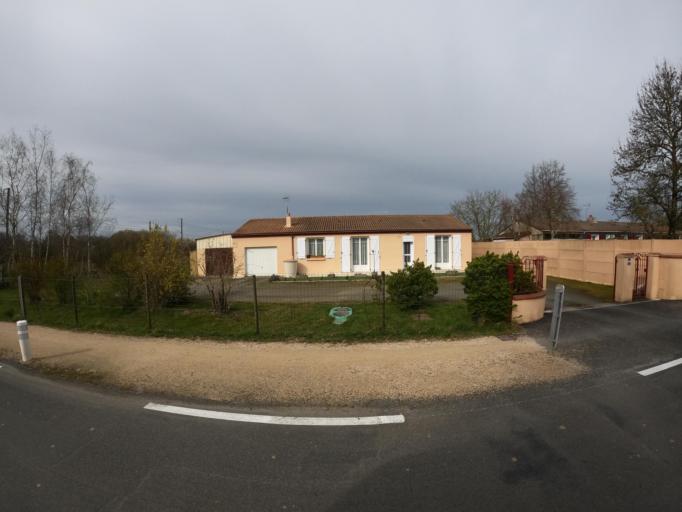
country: FR
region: Pays de la Loire
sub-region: Departement de la Vendee
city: Bouffere
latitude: 46.9569
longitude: -1.3274
